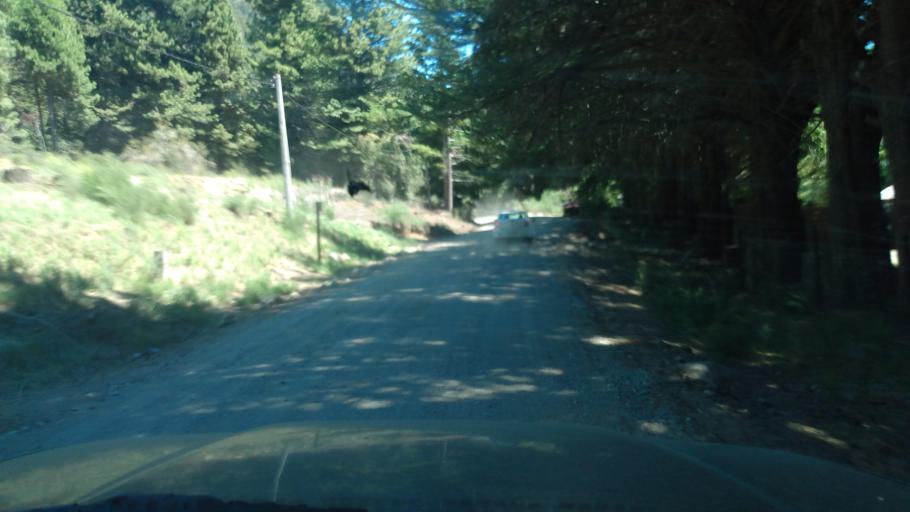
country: AR
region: Rio Negro
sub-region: Departamento de Bariloche
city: San Carlos de Bariloche
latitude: -41.1014
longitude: -71.4959
